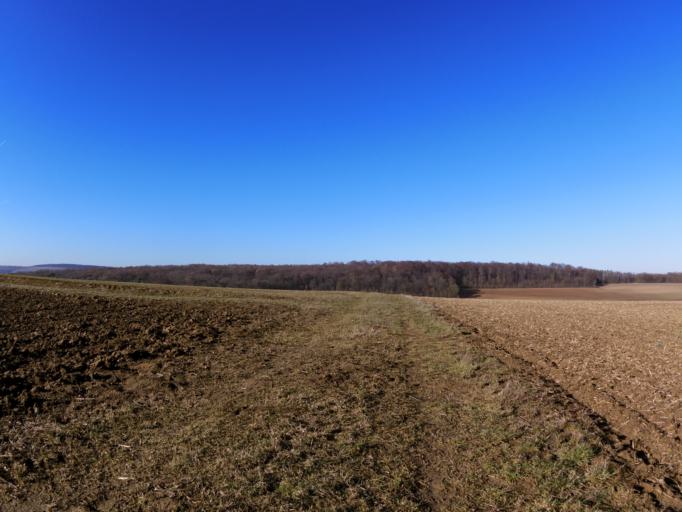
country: DE
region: Bavaria
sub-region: Regierungsbezirk Unterfranken
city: Estenfeld
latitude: 49.8469
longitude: 9.9946
